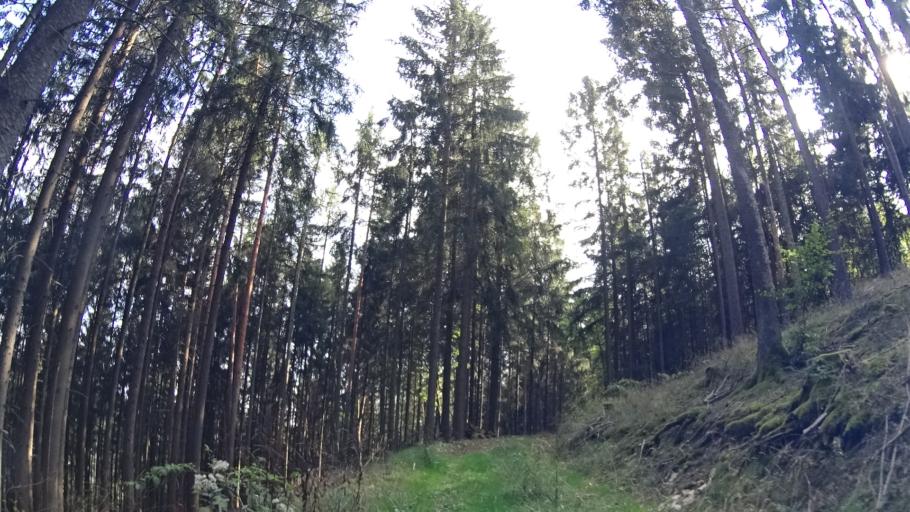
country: DE
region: Bavaria
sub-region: Lower Bavaria
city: Riedenburg
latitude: 48.9832
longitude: 11.6802
